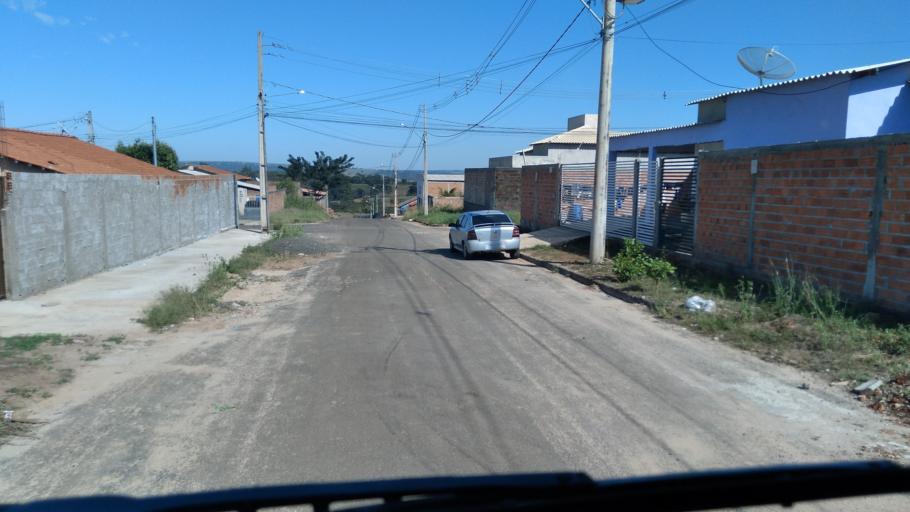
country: BR
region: Goias
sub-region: Mineiros
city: Mineiros
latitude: -17.5768
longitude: -52.5755
